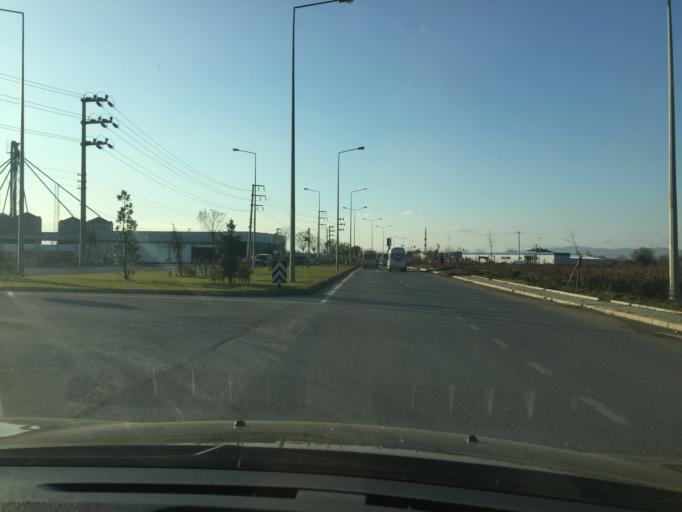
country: TR
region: Sakarya
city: Sogutlu
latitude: 40.9048
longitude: 30.4877
